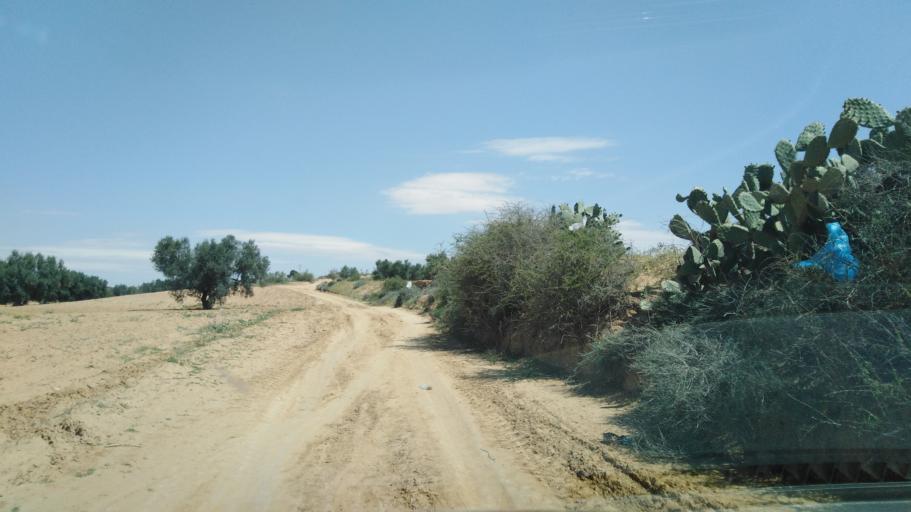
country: TN
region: Safaqis
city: Sfax
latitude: 34.7815
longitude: 10.5281
